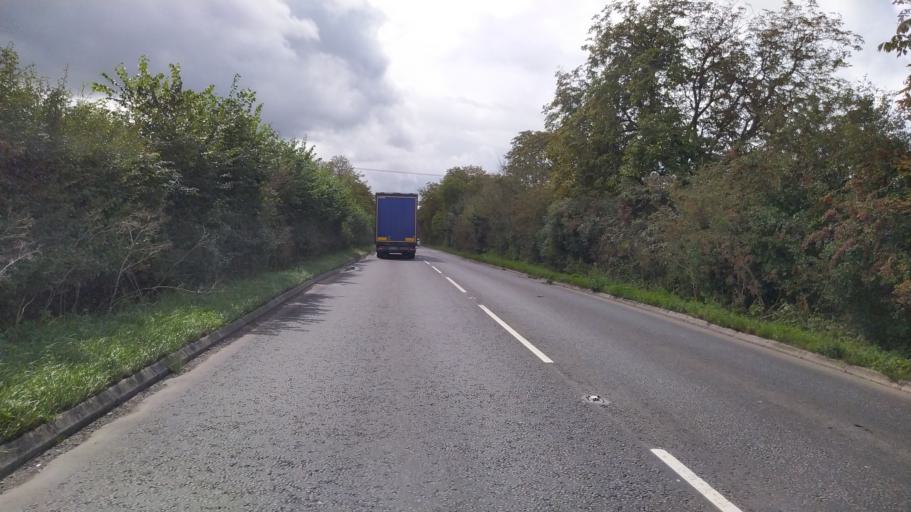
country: GB
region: England
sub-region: Wiltshire
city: Trowbridge
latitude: 51.3215
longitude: -2.1601
